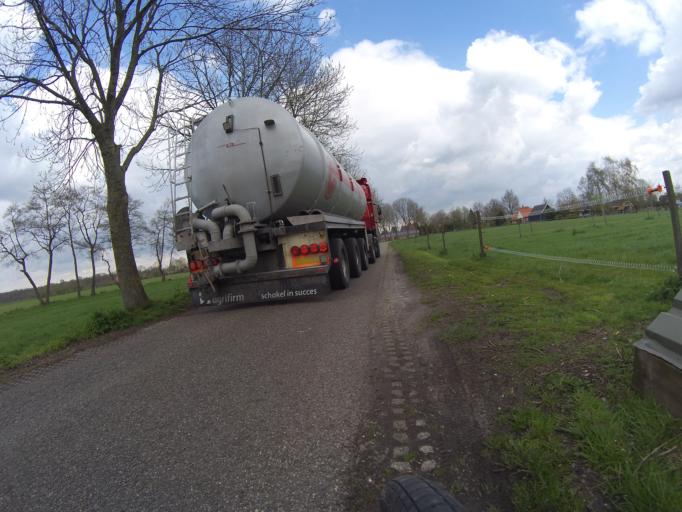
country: NL
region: Gelderland
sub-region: Gemeente Nijkerk
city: Nijkerk
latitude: 52.1886
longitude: 5.4553
